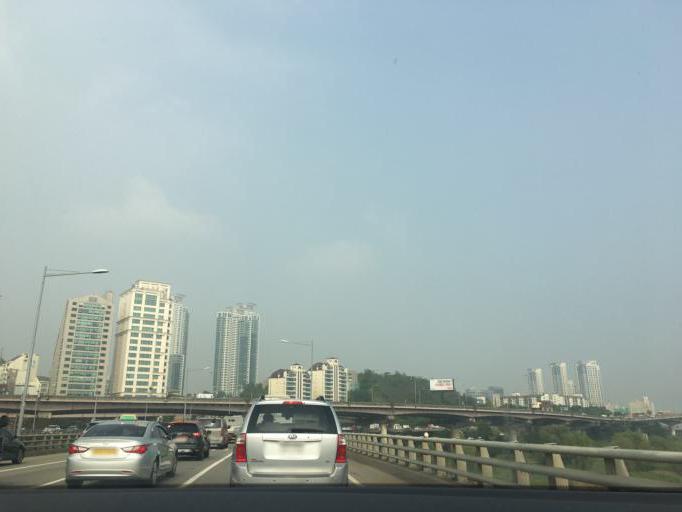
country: KR
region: Seoul
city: Seoul
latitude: 37.5185
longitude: 127.0686
